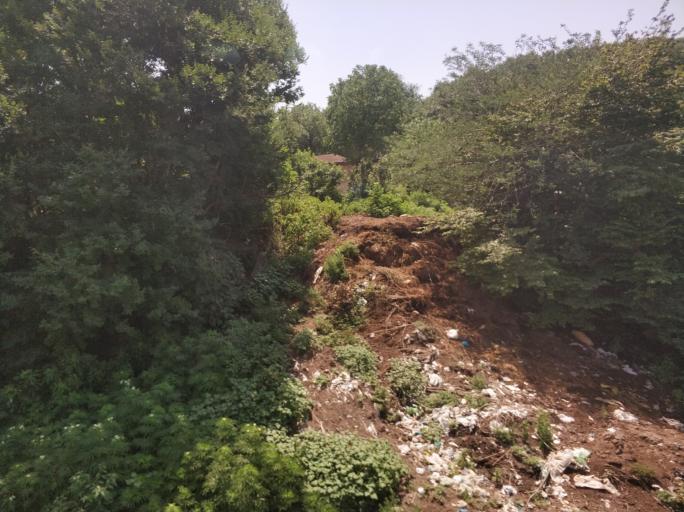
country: IR
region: Gilan
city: Pa'in-e Bazar-e Rudbar
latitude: 37.0065
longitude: 49.5957
